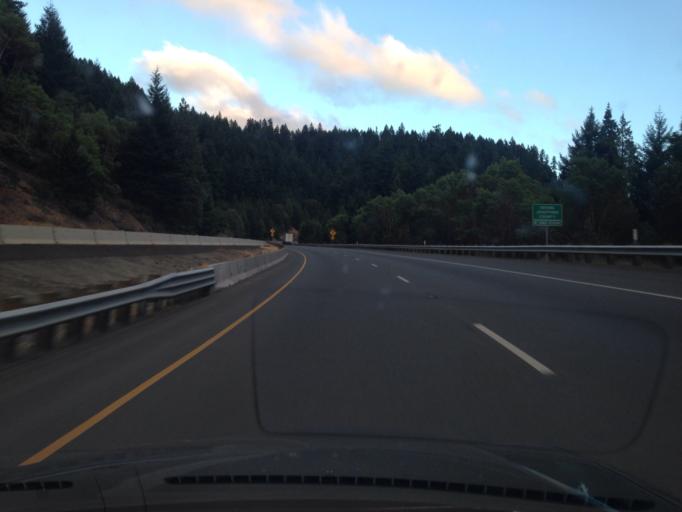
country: US
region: Oregon
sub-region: Douglas County
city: Canyonville
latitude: 42.7405
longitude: -123.3725
